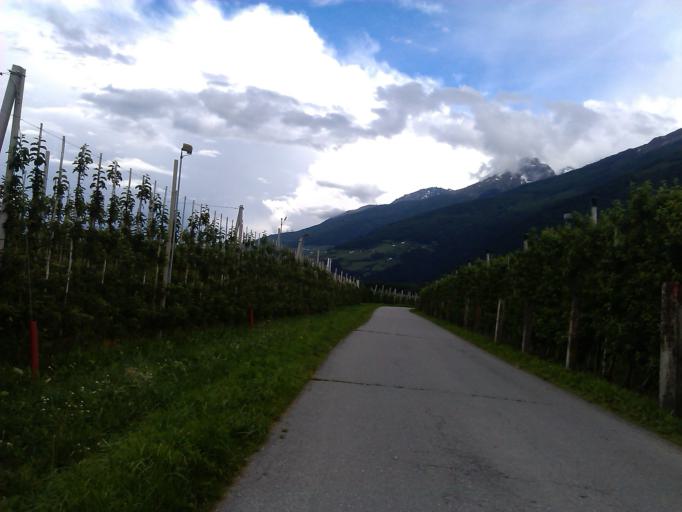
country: IT
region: Trentino-Alto Adige
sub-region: Bolzano
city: Prato Allo Stelvio
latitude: 46.6252
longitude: 10.6221
